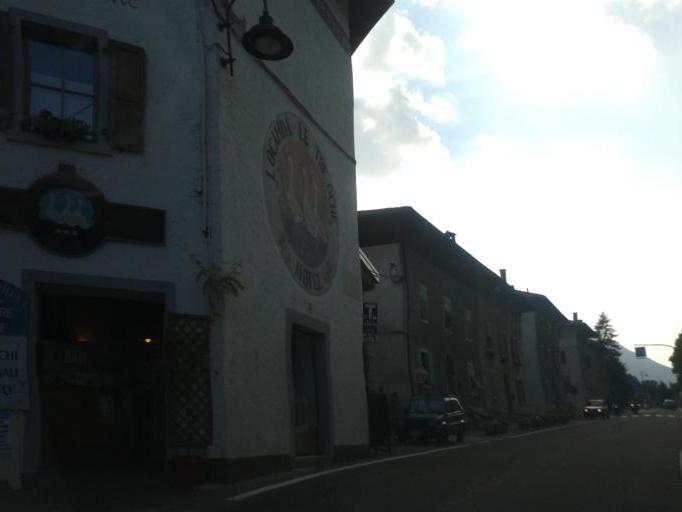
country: IT
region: Trentino-Alto Adige
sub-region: Provincia di Trento
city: Molina di Ledro
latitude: 45.8715
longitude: 10.7732
